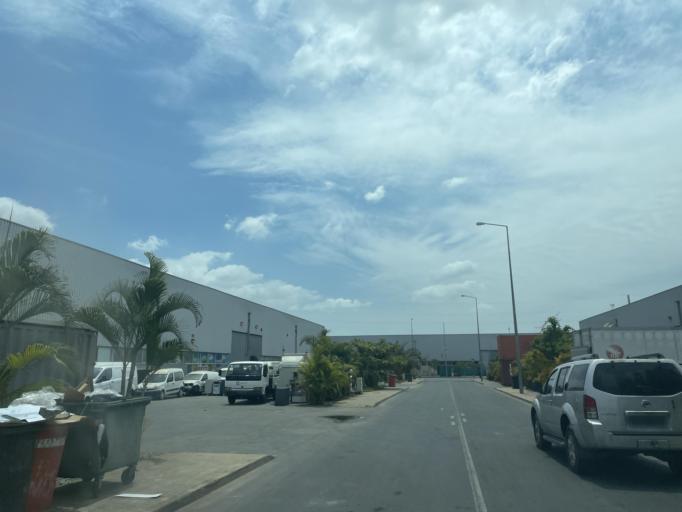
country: AO
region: Luanda
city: Luanda
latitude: -8.9594
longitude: 13.3904
